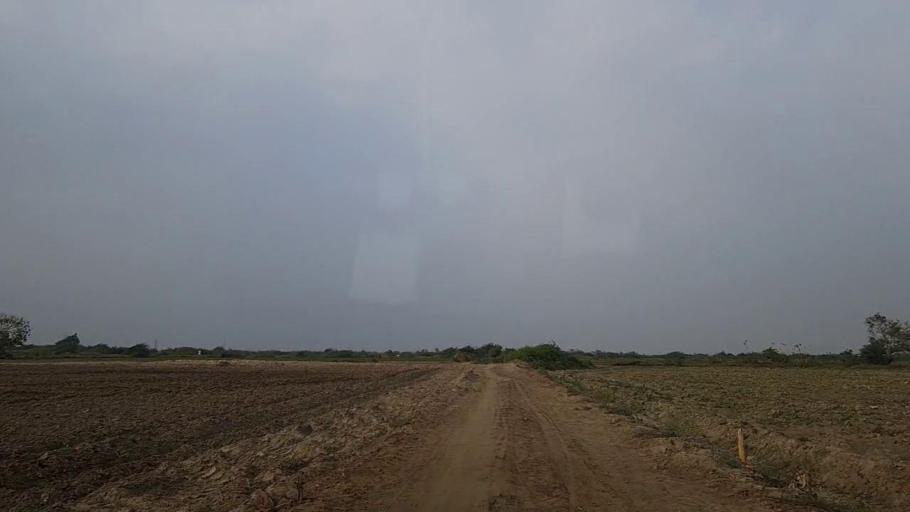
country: PK
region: Sindh
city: Mirpur Sakro
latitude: 24.6179
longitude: 67.5040
